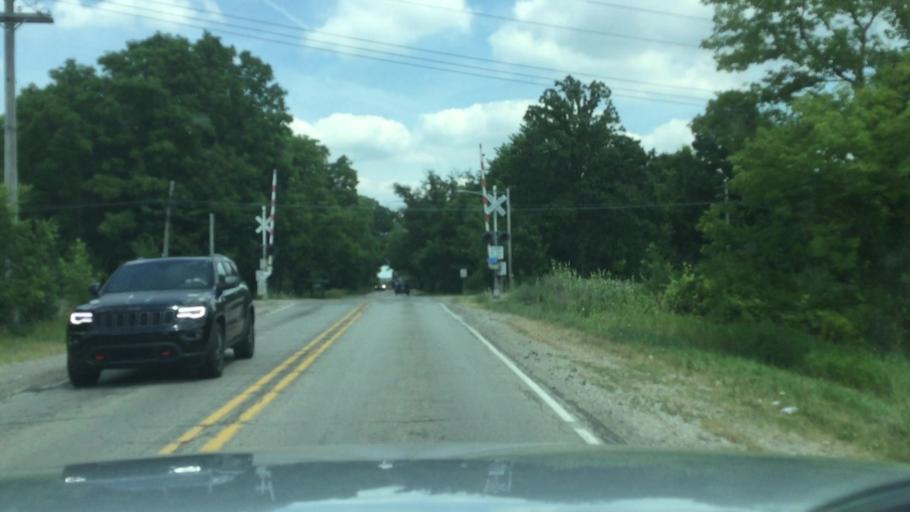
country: US
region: Michigan
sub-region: Genesee County
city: Grand Blanc
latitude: 42.9447
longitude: -83.6425
